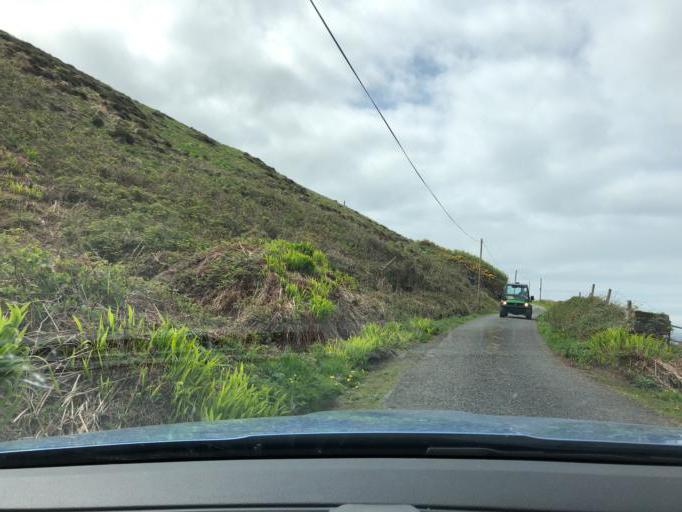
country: IE
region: Connaught
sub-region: County Galway
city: Bearna
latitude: 53.0022
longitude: -9.3916
